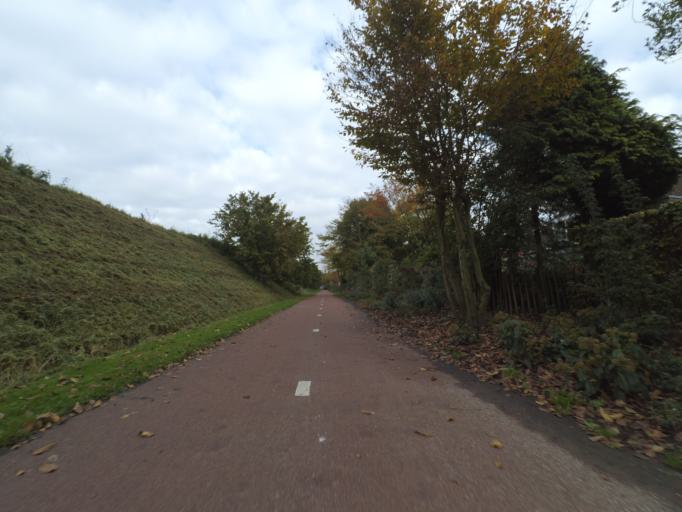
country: NL
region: Gelderland
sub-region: Gemeente Nijkerk
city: Nijkerk
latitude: 52.2206
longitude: 5.4724
